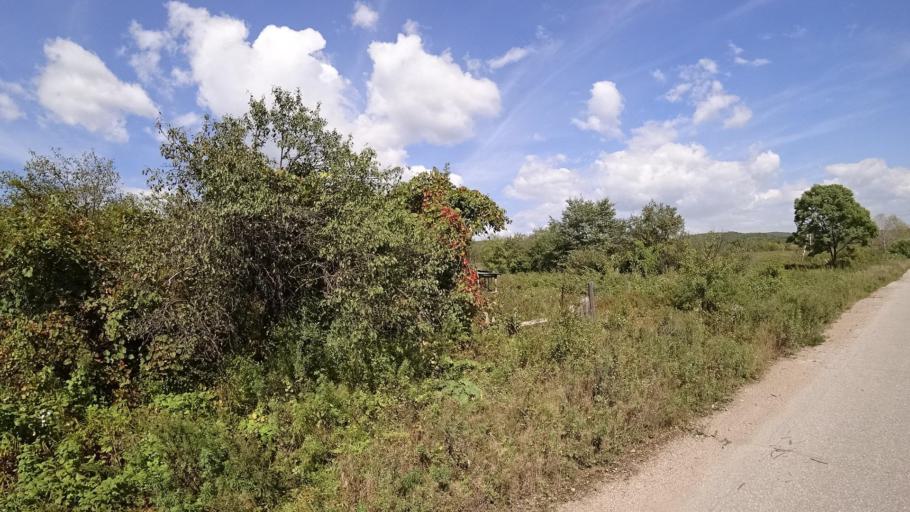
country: RU
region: Jewish Autonomous Oblast
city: Londoko
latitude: 49.0112
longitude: 131.9549
